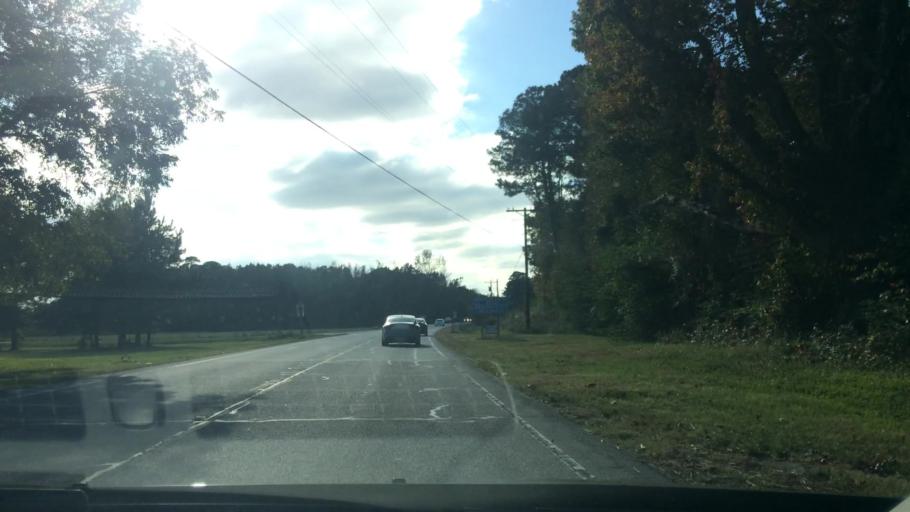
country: US
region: North Carolina
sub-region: Greene County
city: Snow Hill
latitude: 35.4411
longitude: -77.7504
